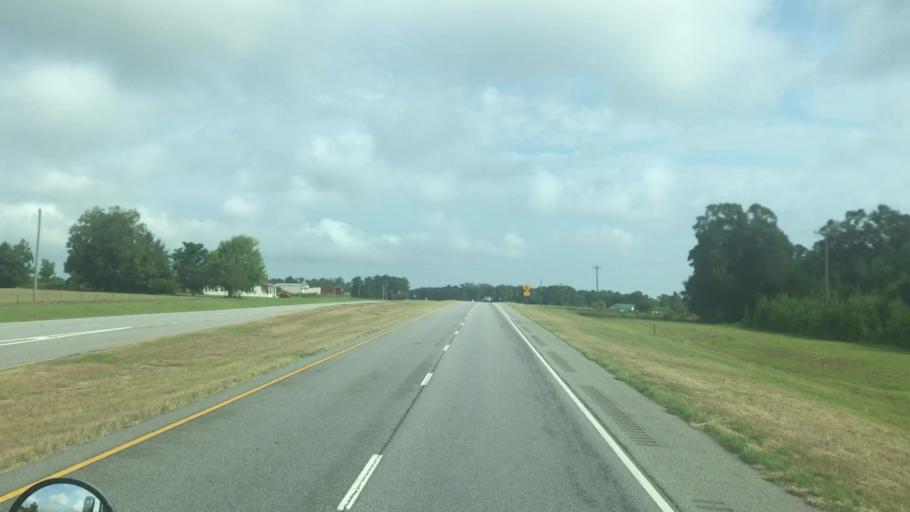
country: US
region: Georgia
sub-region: Miller County
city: Colquitt
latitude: 31.2364
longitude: -84.7858
